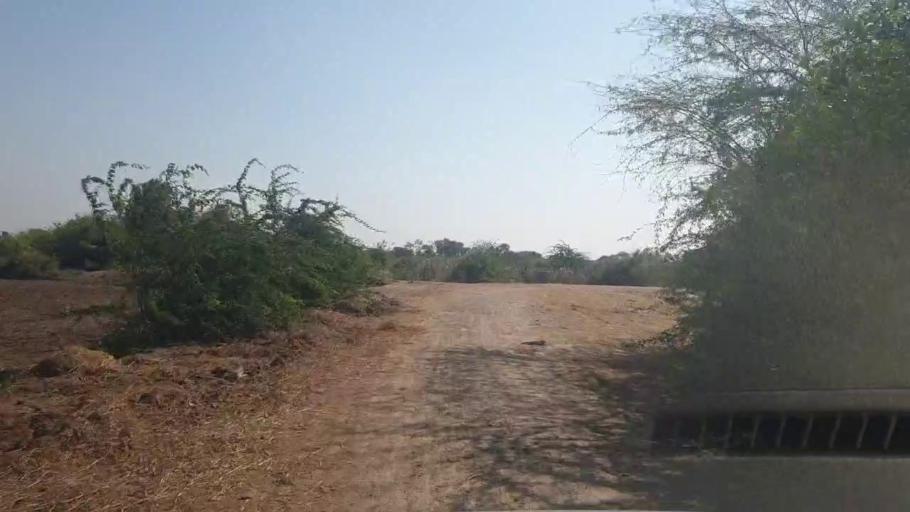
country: PK
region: Sindh
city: Badin
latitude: 24.5452
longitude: 68.8450
